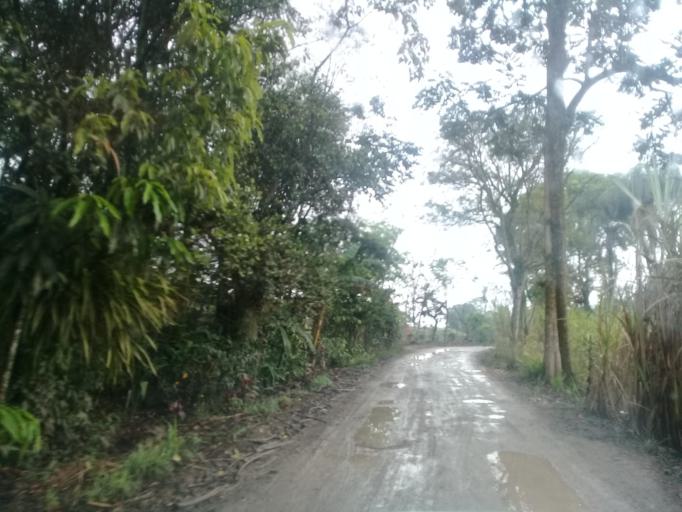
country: MX
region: Veracruz
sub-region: Amatlan de los Reyes
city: Centro de Readaptacion Social
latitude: 18.8209
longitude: -96.9438
